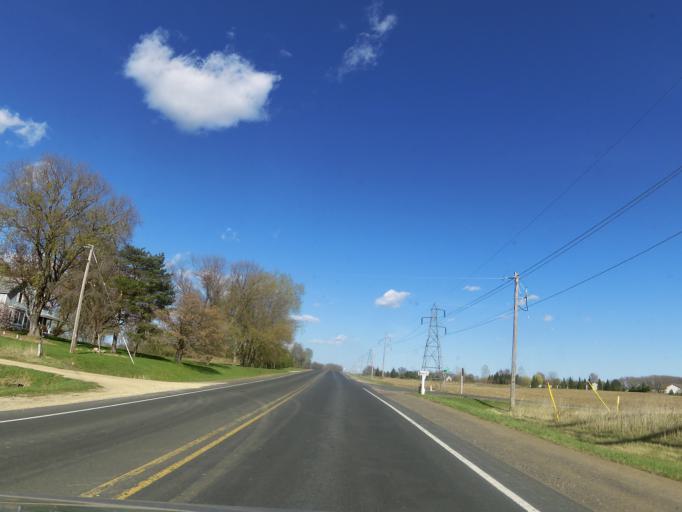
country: US
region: Wisconsin
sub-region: Saint Croix County
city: North Hudson
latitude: 45.0355
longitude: -92.6786
